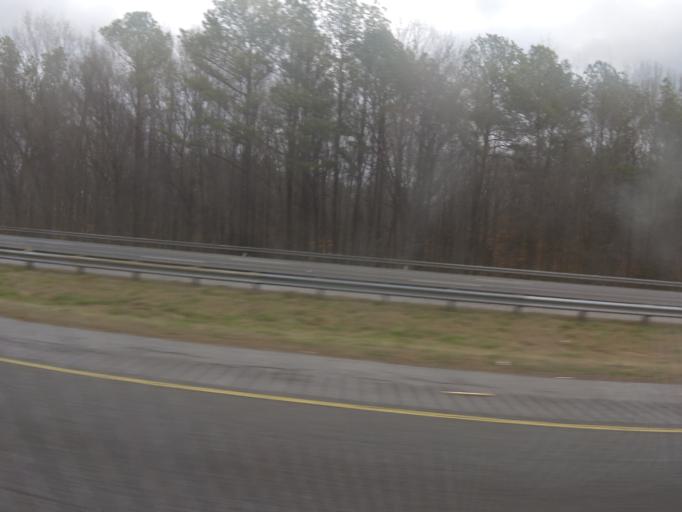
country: US
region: Georgia
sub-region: Whitfield County
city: Dalton
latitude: 34.6753
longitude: -84.9985
